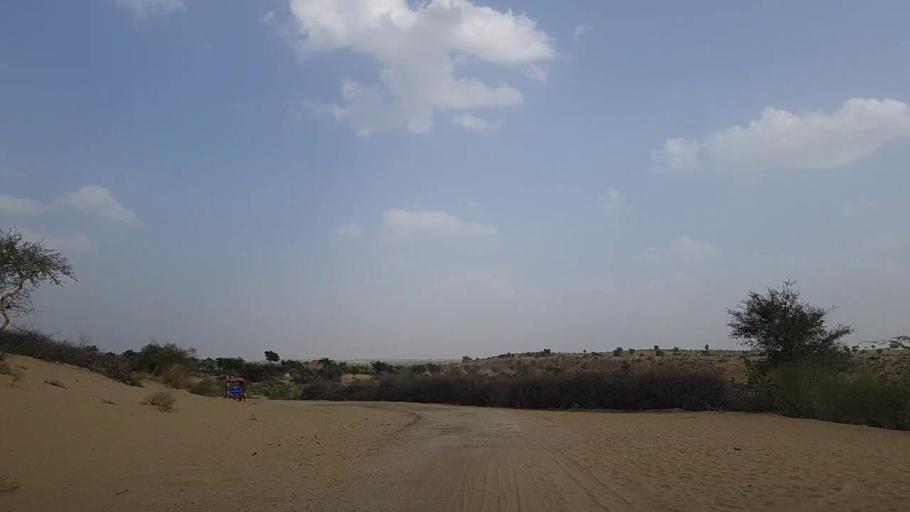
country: PK
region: Sindh
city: Islamkot
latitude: 24.7683
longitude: 70.1754
